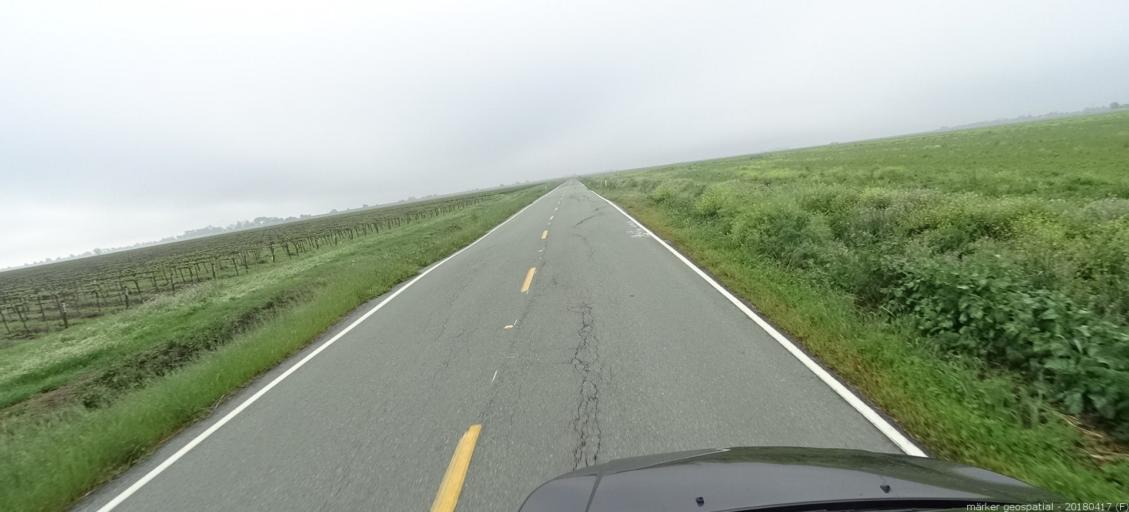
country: US
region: California
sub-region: Sacramento County
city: Walnut Grove
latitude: 38.2157
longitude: -121.5282
